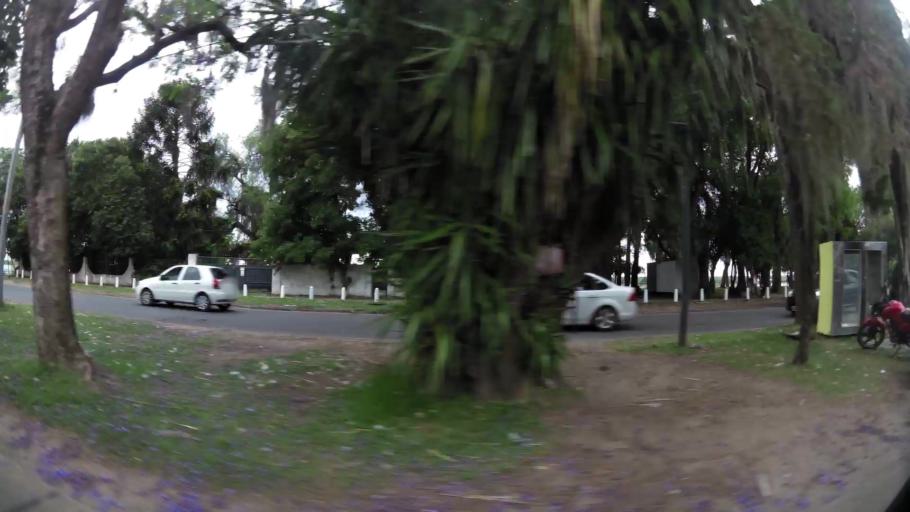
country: AR
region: Santa Fe
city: Granadero Baigorria
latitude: -32.8755
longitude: -60.6885
